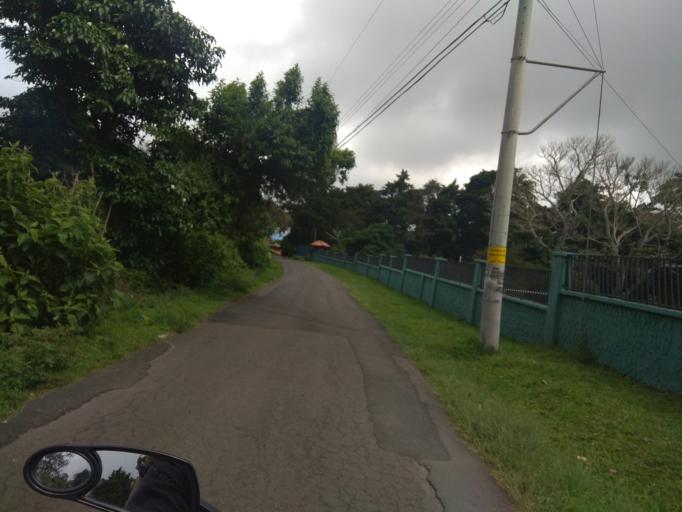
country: CR
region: Heredia
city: San Josecito
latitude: 10.0348
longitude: -84.0971
